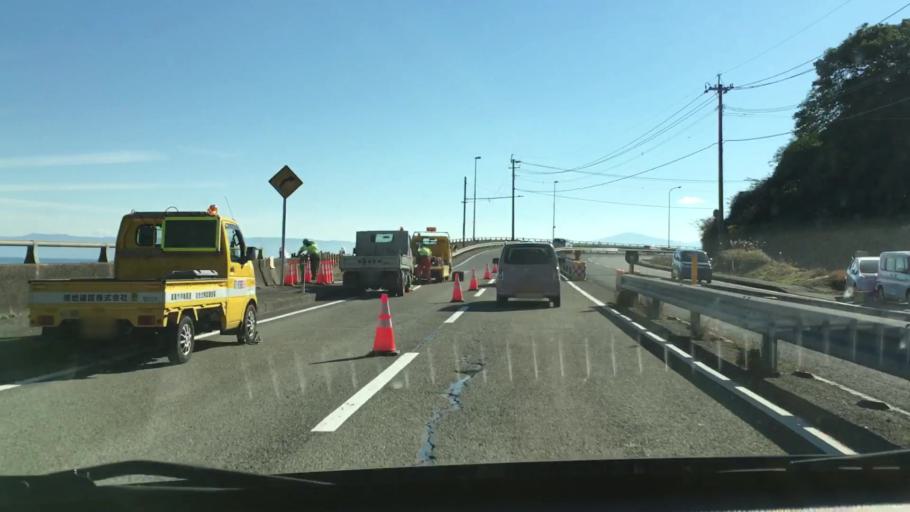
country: JP
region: Kagoshima
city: Kajiki
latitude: 31.6595
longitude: 130.6181
